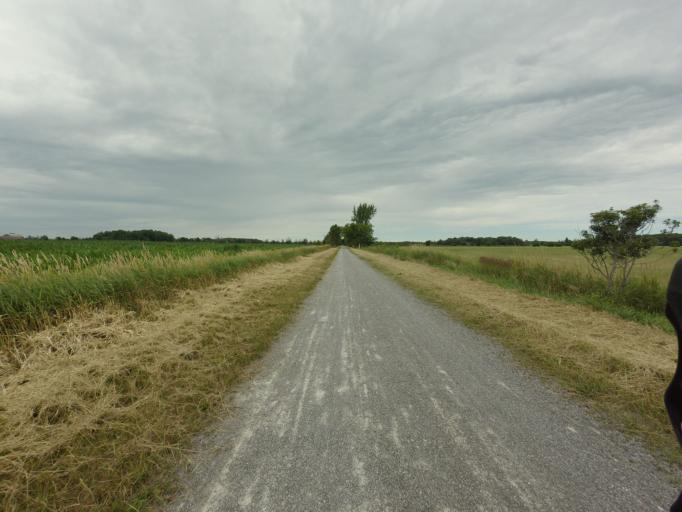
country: CA
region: Ontario
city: Ottawa
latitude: 45.1606
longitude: -75.6150
